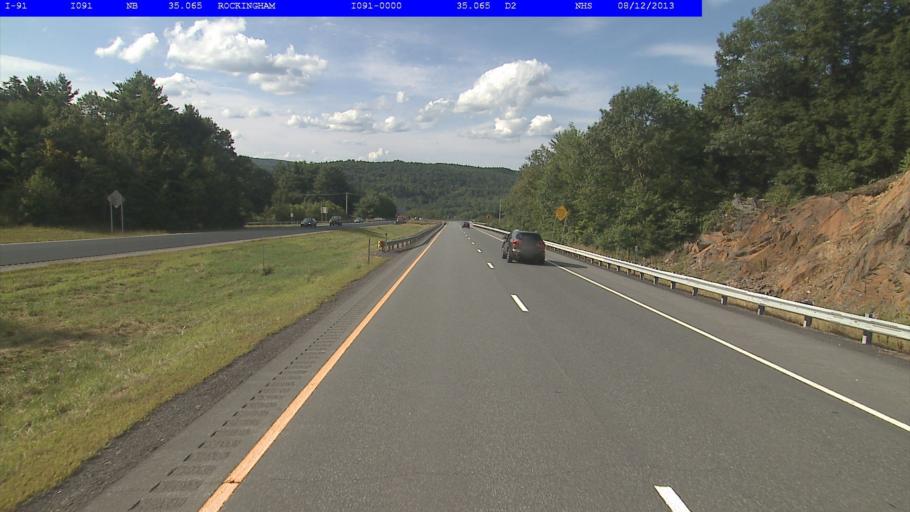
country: US
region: Vermont
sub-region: Windham County
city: Rockingham
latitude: 43.1767
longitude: -72.4628
